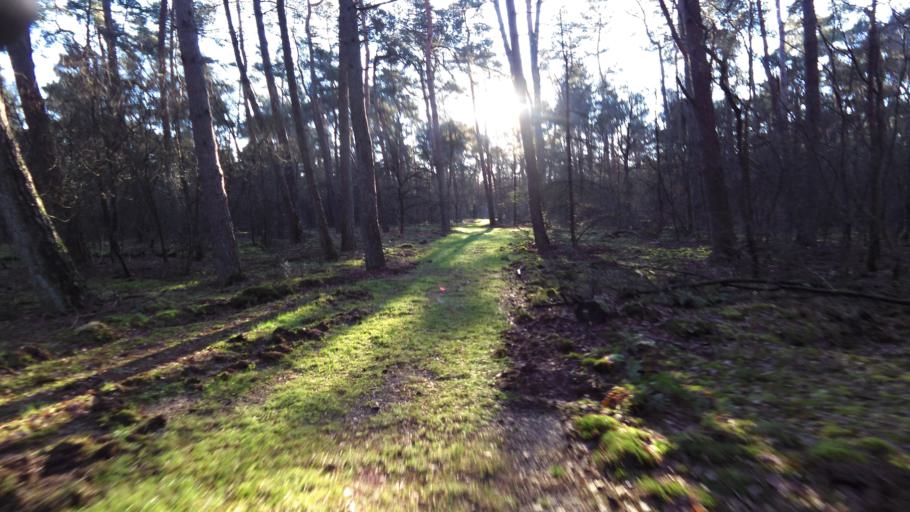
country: NL
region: Gelderland
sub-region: Gemeente Barneveld
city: Garderen
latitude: 52.2119
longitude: 5.7190
